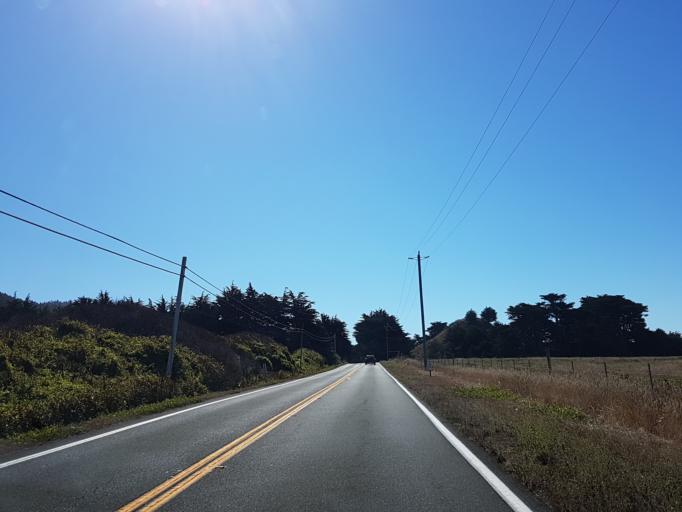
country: US
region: California
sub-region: Mendocino County
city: Boonville
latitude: 39.0965
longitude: -123.7043
